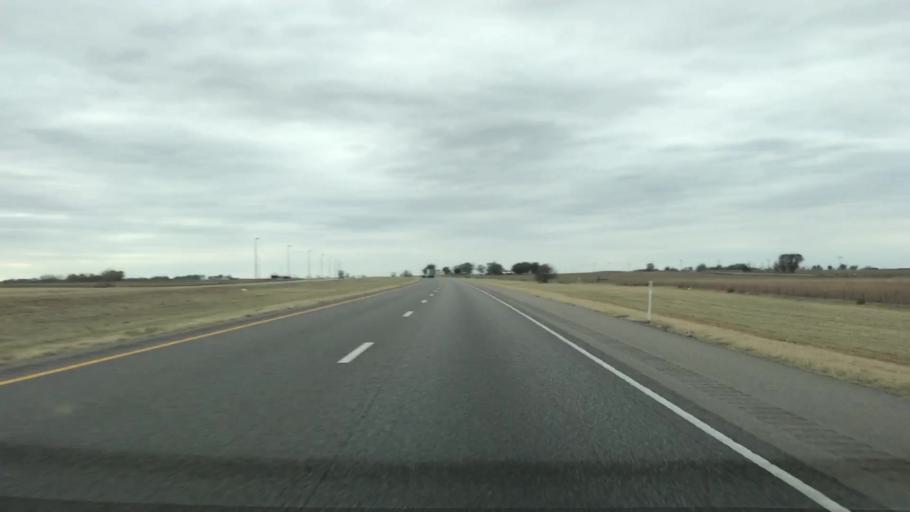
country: US
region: Oklahoma
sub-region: Beckham County
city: Erick
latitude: 35.2322
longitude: -99.9538
